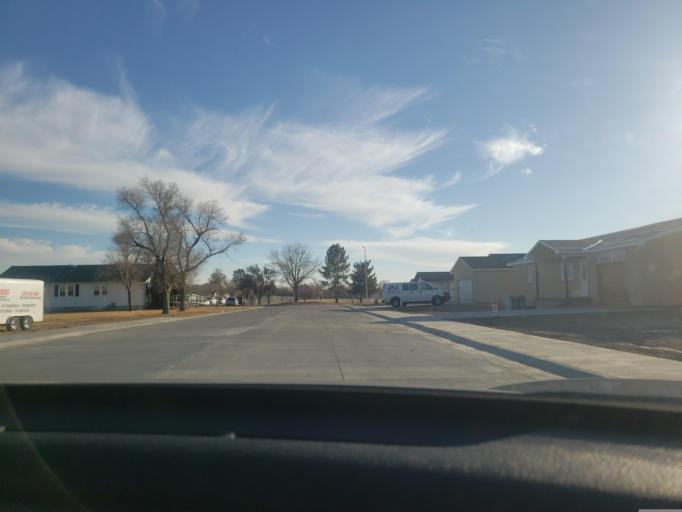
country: US
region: Kansas
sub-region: Finney County
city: Garden City
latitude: 37.9867
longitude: -100.8776
